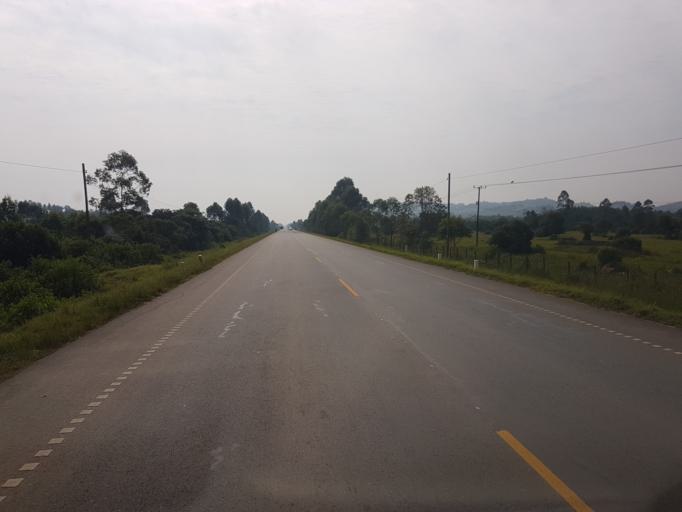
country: UG
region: Western Region
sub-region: Sheema District
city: Kibingo
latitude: -0.6476
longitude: 30.4893
